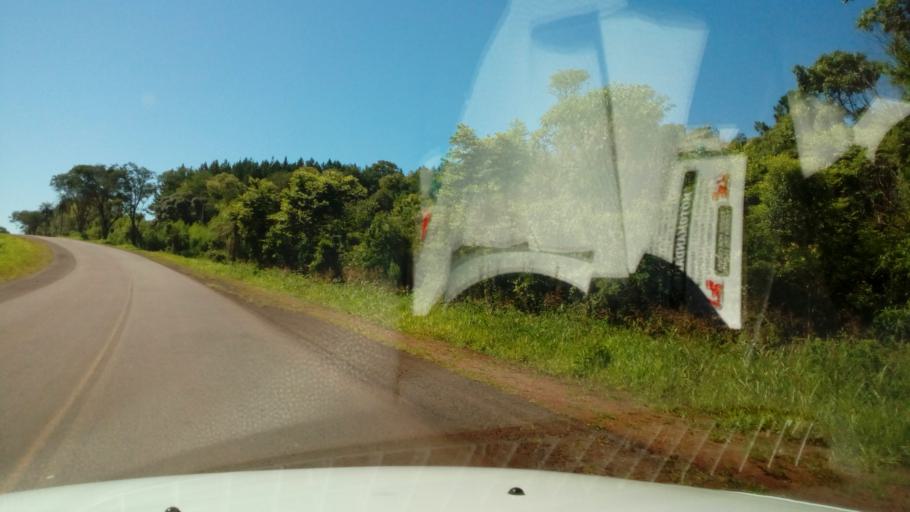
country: AR
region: Misiones
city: Almafuerte
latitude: -27.5583
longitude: -55.4176
